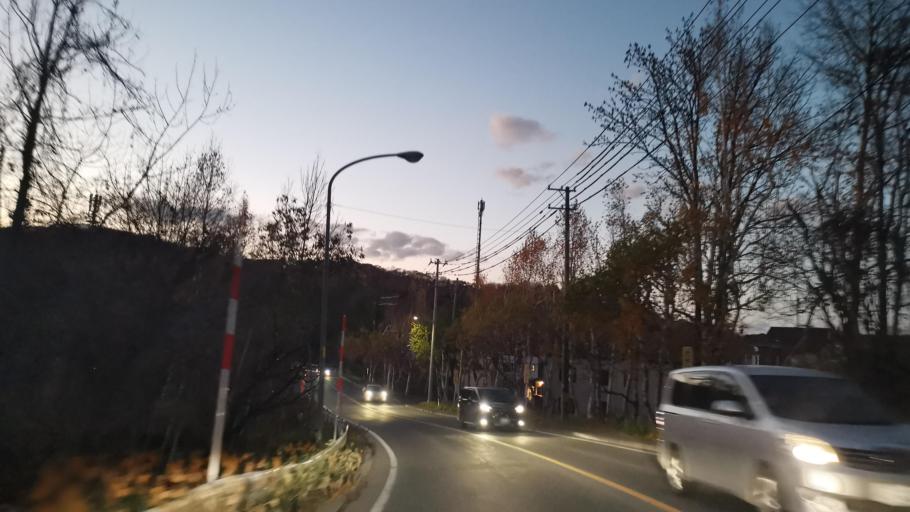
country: JP
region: Hokkaido
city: Sapporo
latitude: 42.9944
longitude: 141.3657
